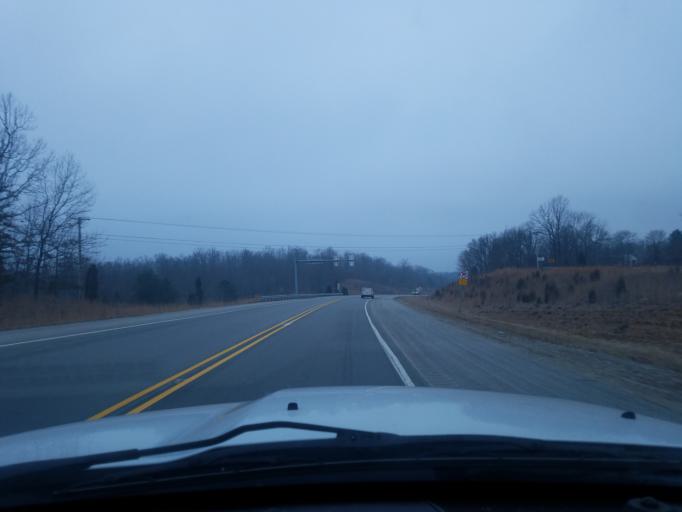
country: US
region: Indiana
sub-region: Perry County
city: Tell City
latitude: 38.0604
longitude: -86.6222
